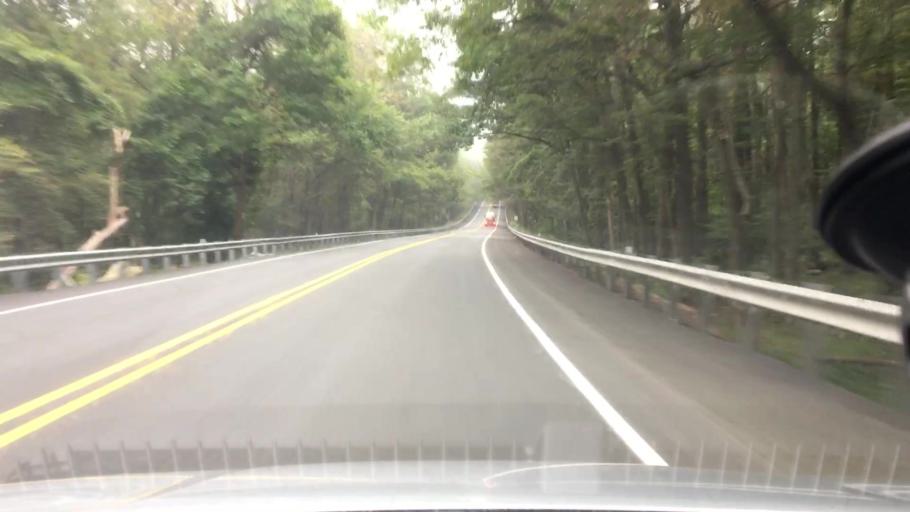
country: US
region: Pennsylvania
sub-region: Monroe County
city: Mount Pocono
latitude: 41.1291
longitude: -75.3378
